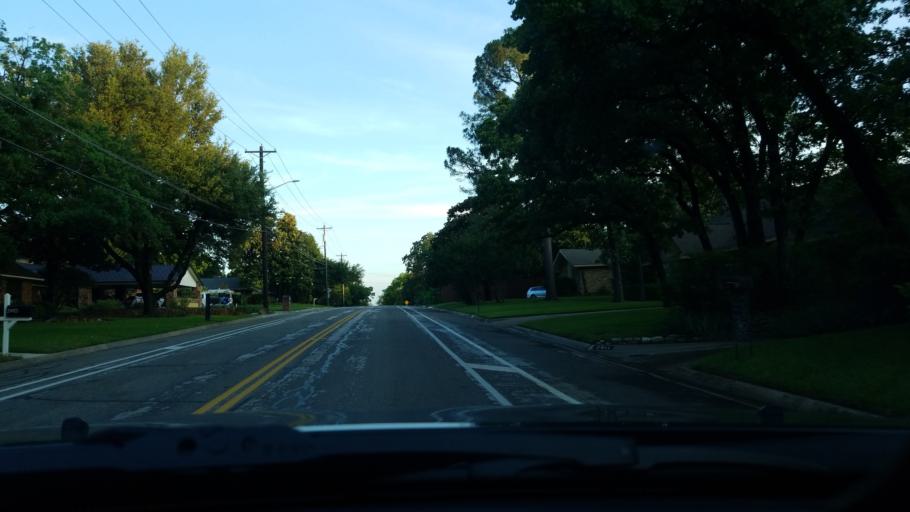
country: US
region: Texas
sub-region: Denton County
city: Denton
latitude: 33.2415
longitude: -97.1067
